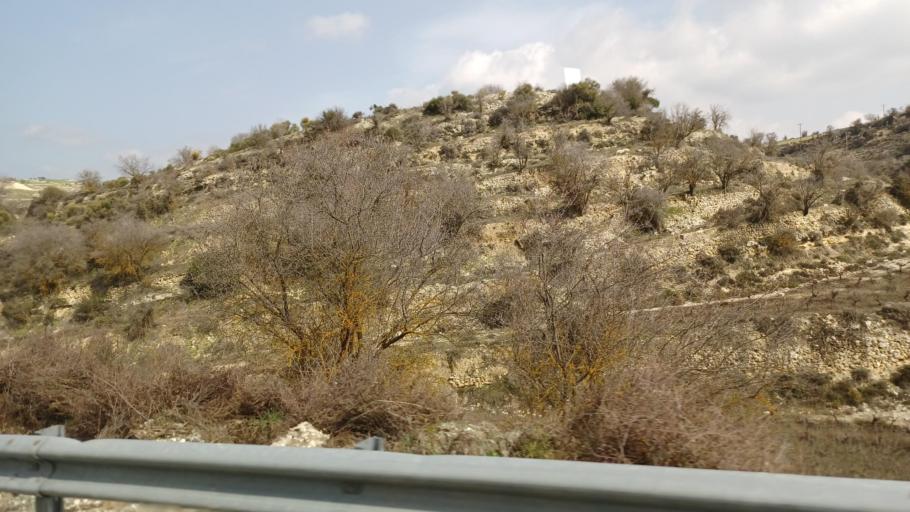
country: CY
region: Limassol
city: Pachna
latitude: 34.8125
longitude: 32.7891
